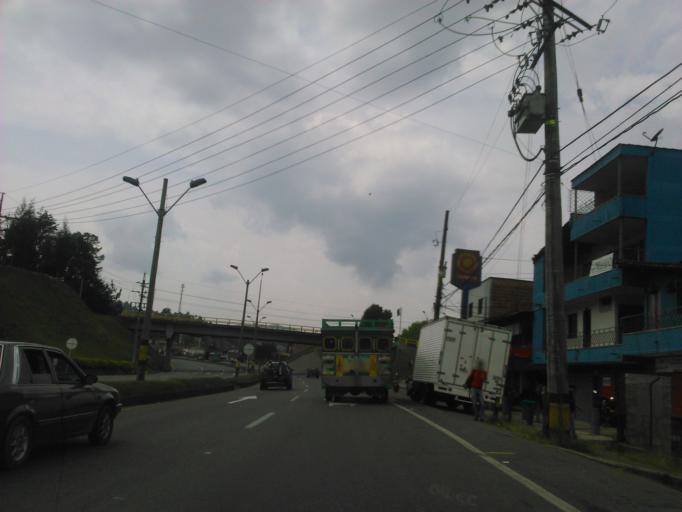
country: CO
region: Antioquia
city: Guarne
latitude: 6.2747
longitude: -75.4407
